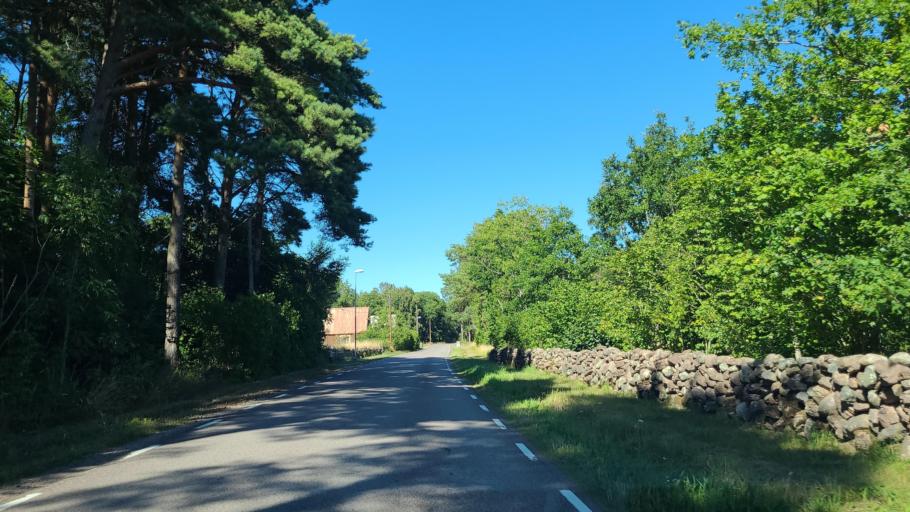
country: SE
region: Kalmar
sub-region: Borgholms Kommun
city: Borgholm
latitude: 56.8313
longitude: 16.7733
